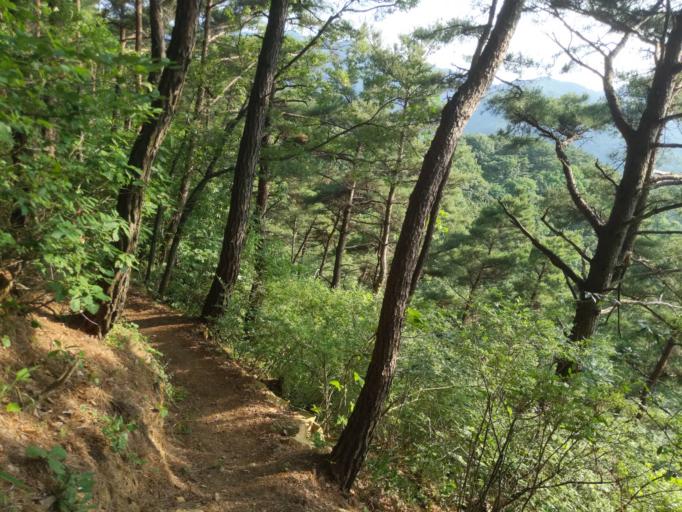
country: KR
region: Daegu
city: Hwawon
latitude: 35.7889
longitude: 128.5404
